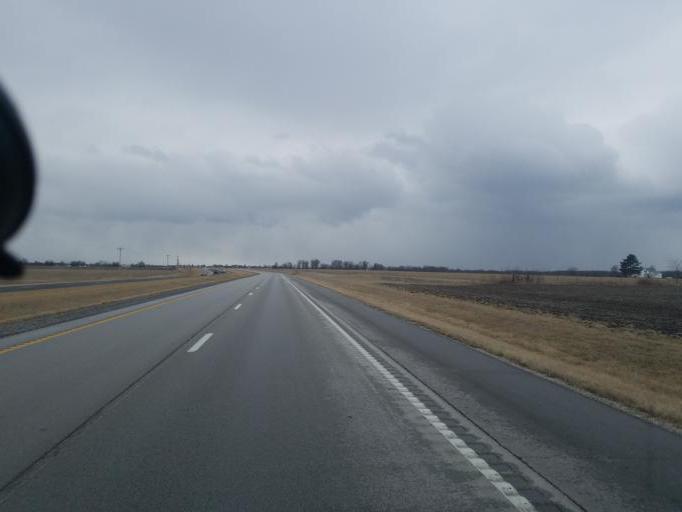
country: US
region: Missouri
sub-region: Macon County
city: Macon
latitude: 39.8142
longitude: -92.4737
